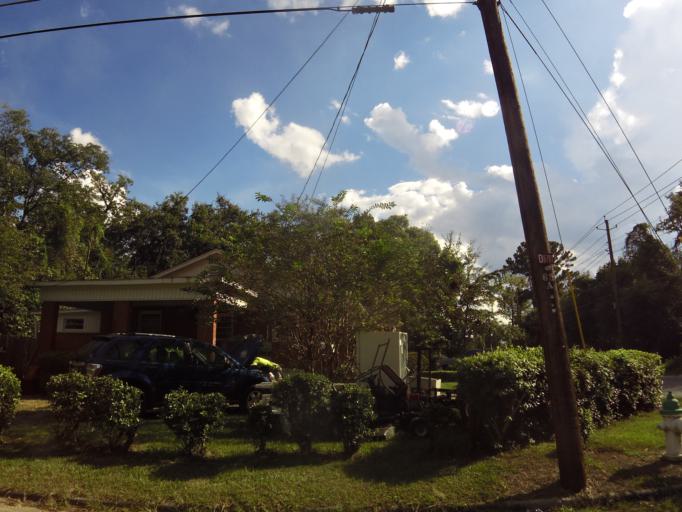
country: US
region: Georgia
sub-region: Lowndes County
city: Valdosta
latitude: 30.8317
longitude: -83.2907
